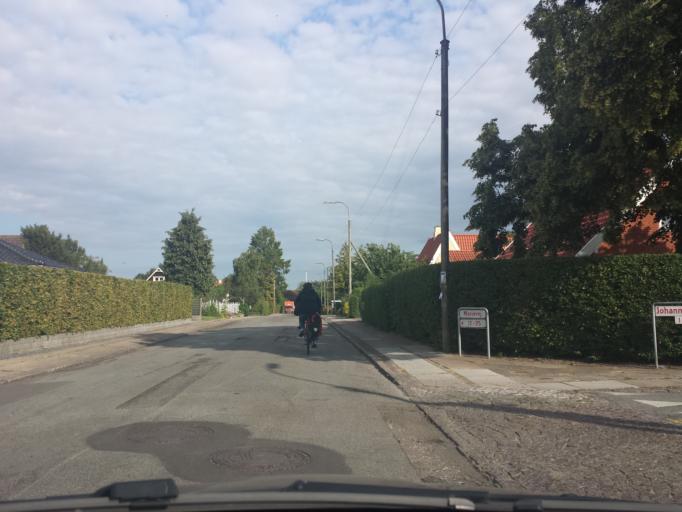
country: DK
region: Capital Region
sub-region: Herlev Kommune
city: Herlev
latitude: 55.7253
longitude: 12.4017
